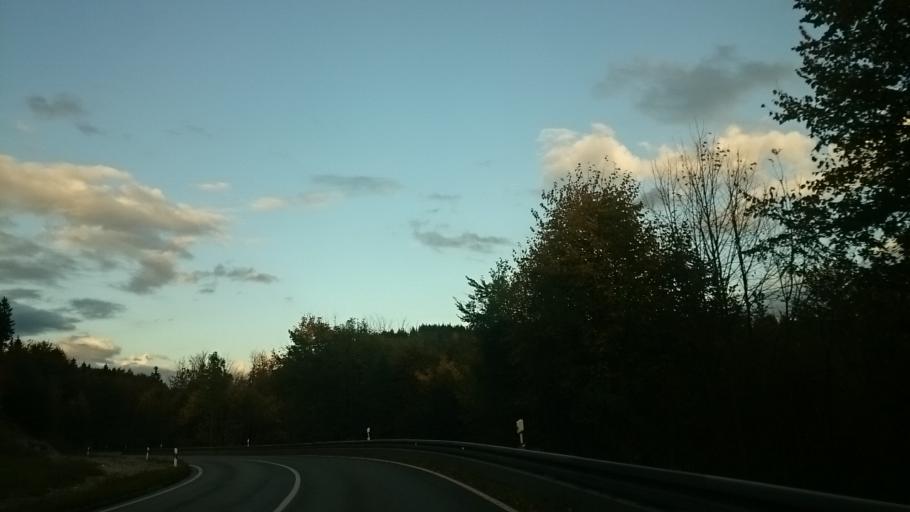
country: DE
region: Bavaria
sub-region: Upper Bavaria
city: Peiting
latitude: 47.7634
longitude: 10.9459
